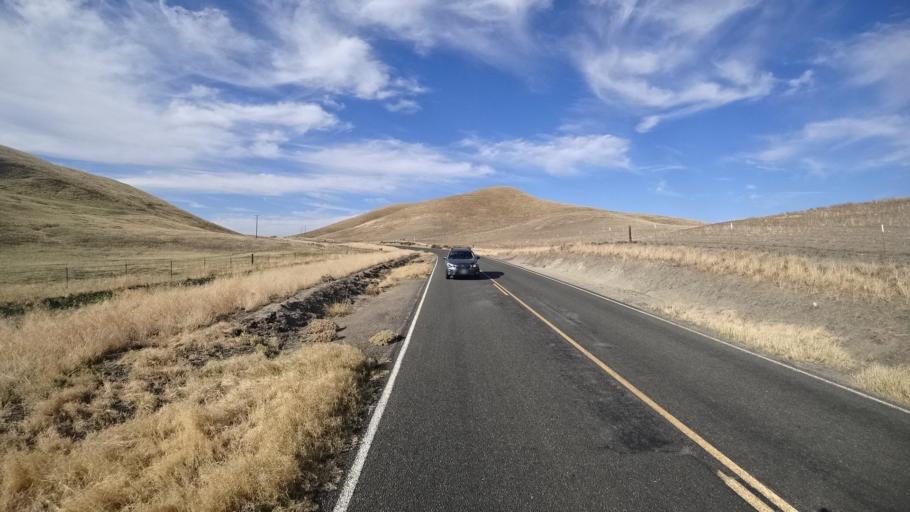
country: US
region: California
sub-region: Kern County
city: Oildale
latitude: 35.6125
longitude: -118.8814
